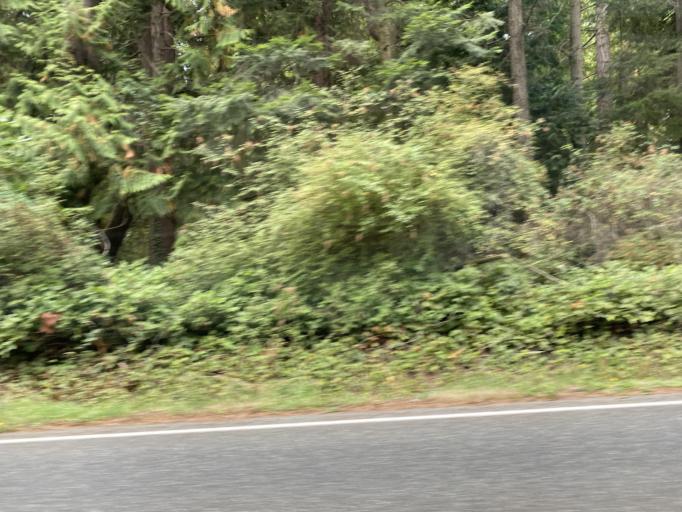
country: US
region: Washington
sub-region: Island County
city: Coupeville
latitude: 48.2213
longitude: -122.7305
